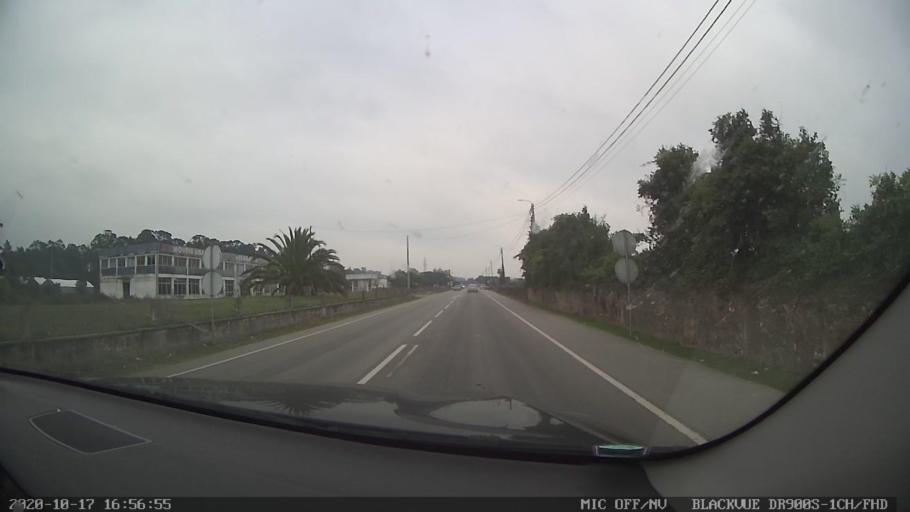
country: PT
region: Braga
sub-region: Esposende
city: Apulia
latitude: 41.5034
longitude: -8.7619
